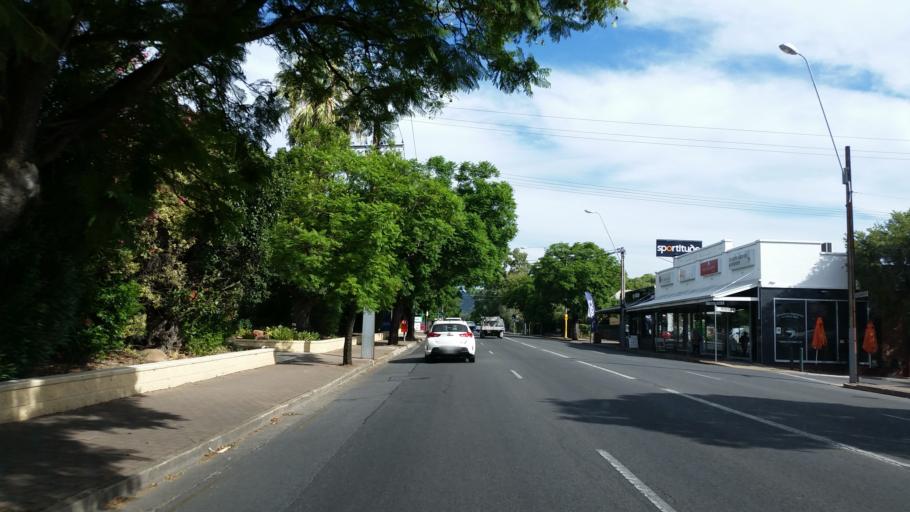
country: AU
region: South Australia
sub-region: Unley
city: Fullarton
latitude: -34.9554
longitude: 138.6258
